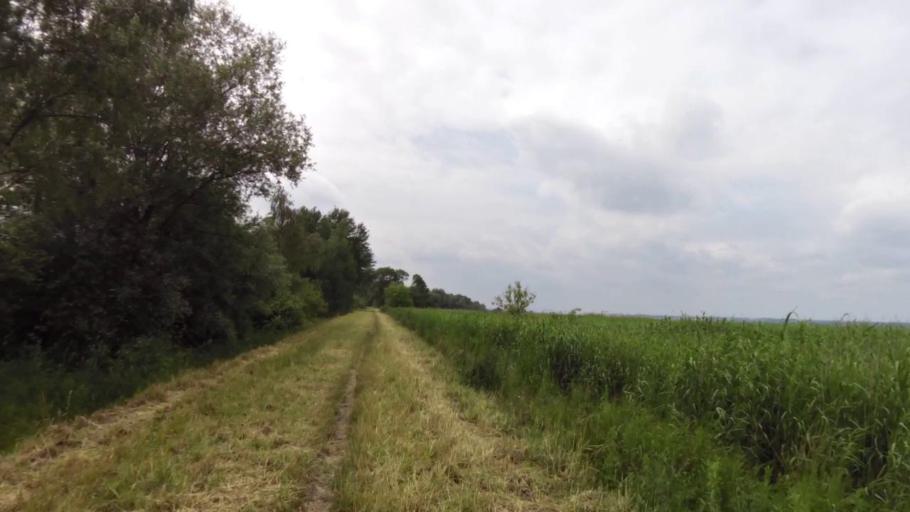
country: PL
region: West Pomeranian Voivodeship
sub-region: Szczecin
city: Szczecin
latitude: 53.4325
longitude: 14.6711
